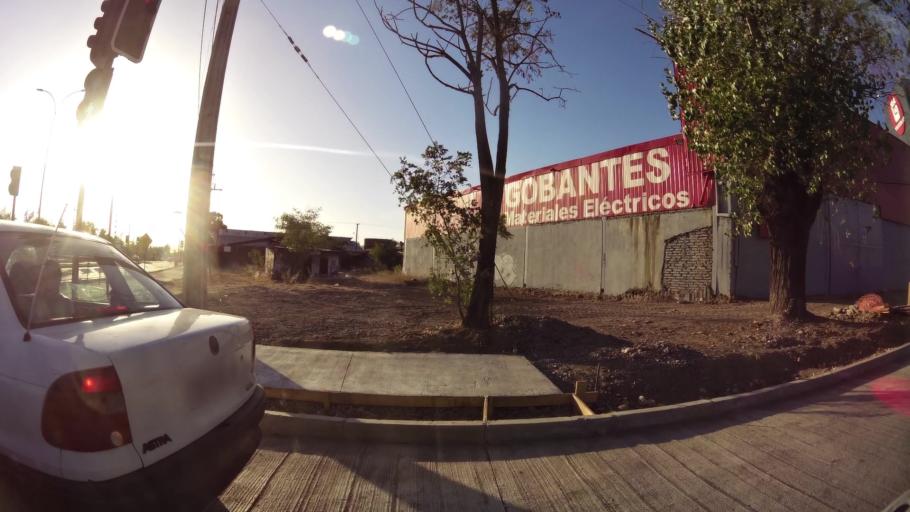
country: CL
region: Maule
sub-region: Provincia de Talca
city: Talca
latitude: -35.4367
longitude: -71.6441
